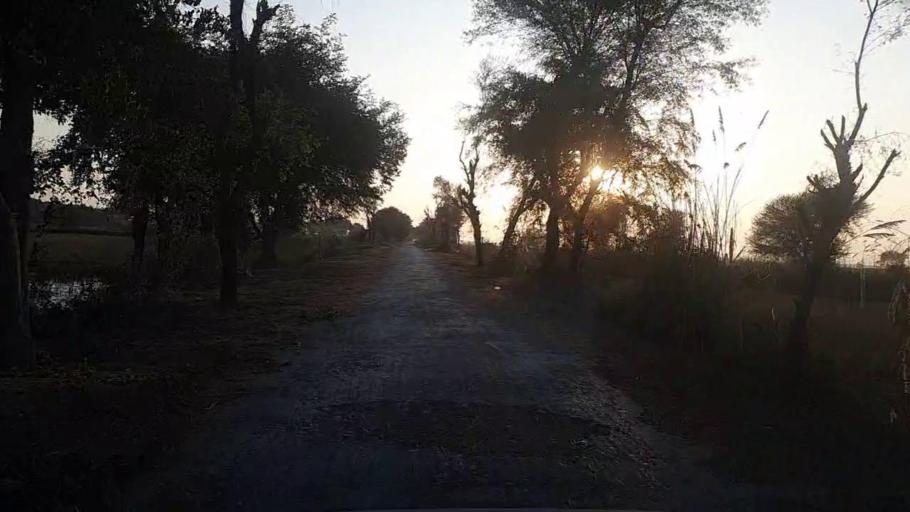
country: PK
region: Sindh
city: Mehar
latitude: 27.1828
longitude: 67.7365
